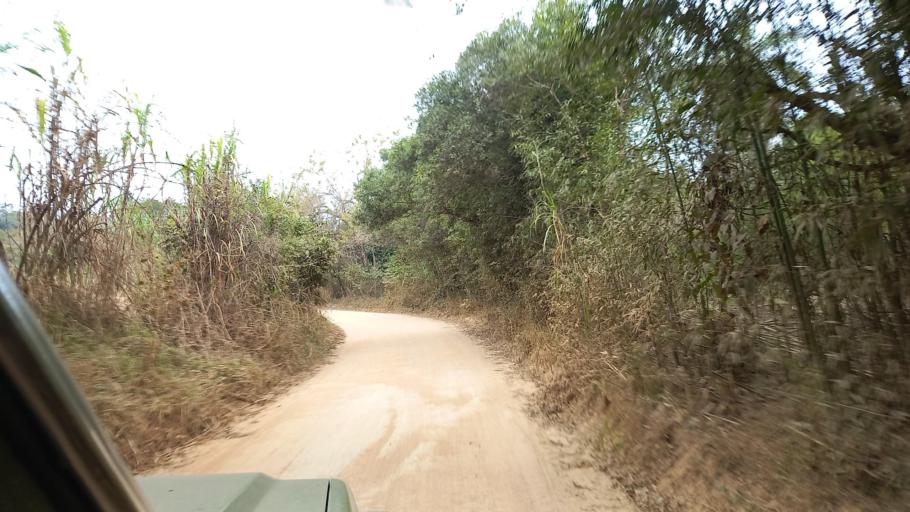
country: BR
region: Sao Paulo
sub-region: Moji-Guacu
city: Mogi-Gaucu
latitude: -22.2989
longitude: -46.8334
